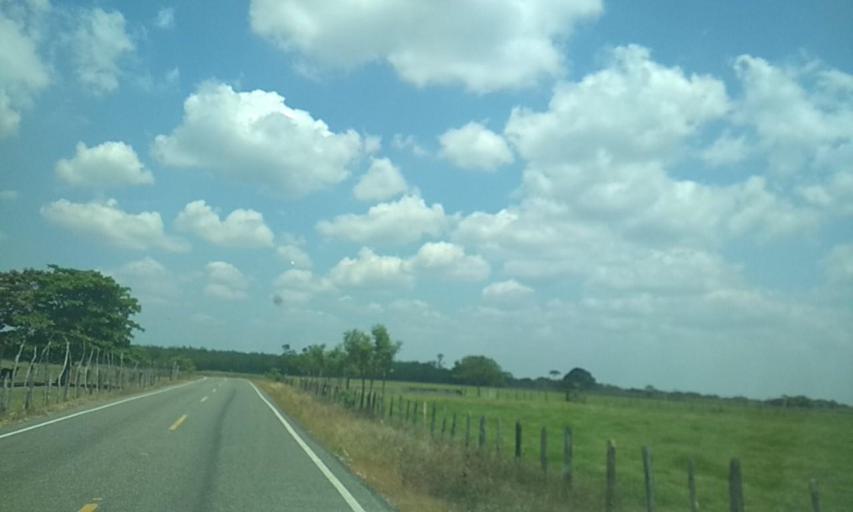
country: MX
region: Tabasco
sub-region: Huimanguillo
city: Huapacal 1ra. Seccion
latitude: 17.7522
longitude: -93.7156
